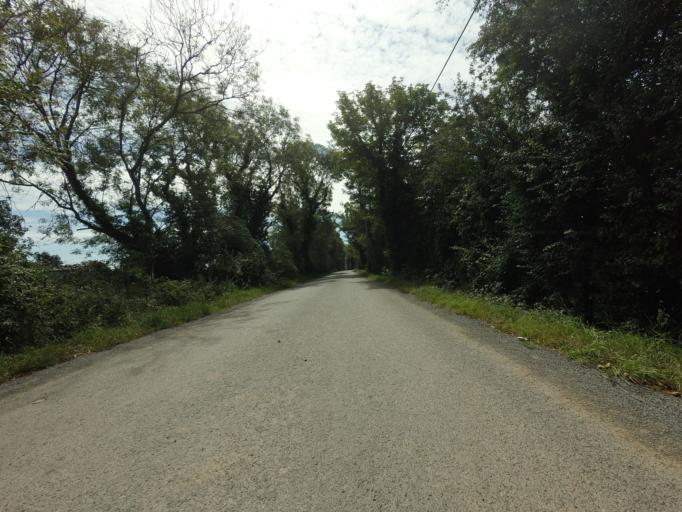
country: GB
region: England
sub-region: Kent
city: Stone
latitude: 50.9950
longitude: 0.8055
